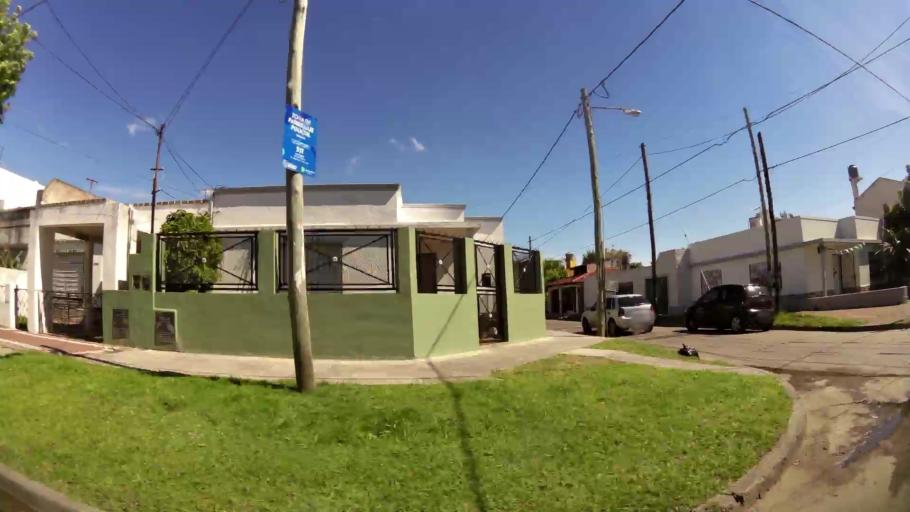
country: AR
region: Buenos Aires
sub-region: Partido de Lomas de Zamora
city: Lomas de Zamora
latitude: -34.7407
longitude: -58.4204
